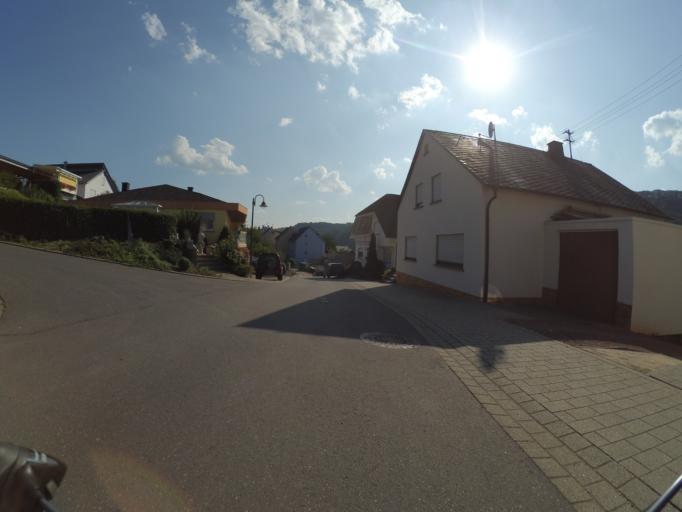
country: DE
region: Rheinland-Pfalz
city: Neumagen-Dhron
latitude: 49.8544
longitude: 6.8978
